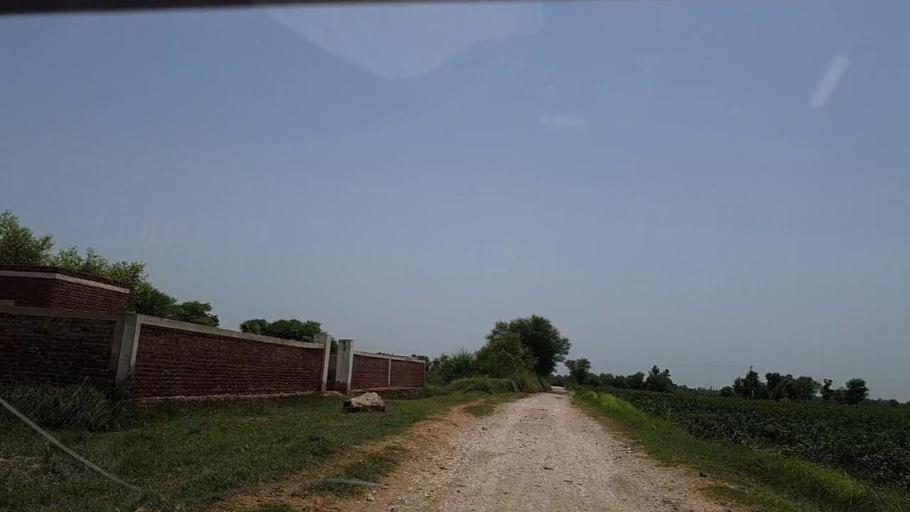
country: PK
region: Sindh
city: Tharu Shah
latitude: 26.9280
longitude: 68.0409
